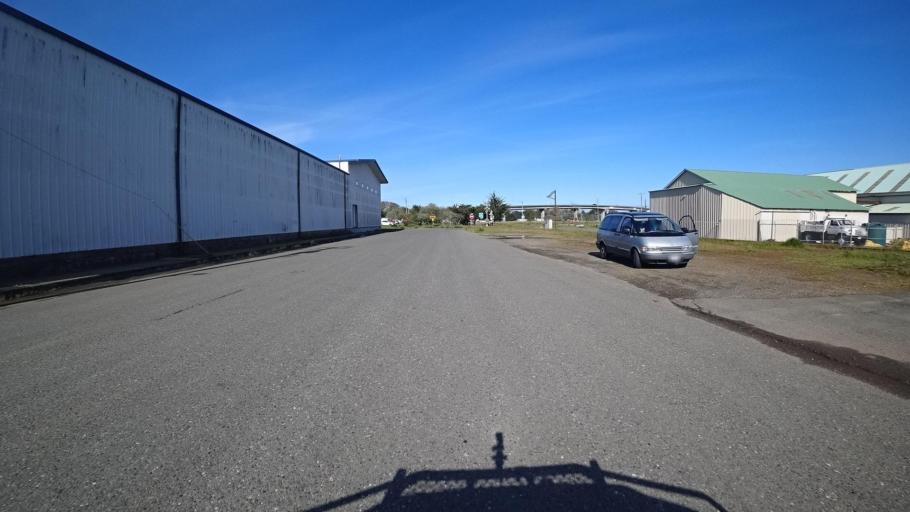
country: US
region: California
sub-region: Humboldt County
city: Eureka
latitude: 40.8072
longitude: -124.1505
